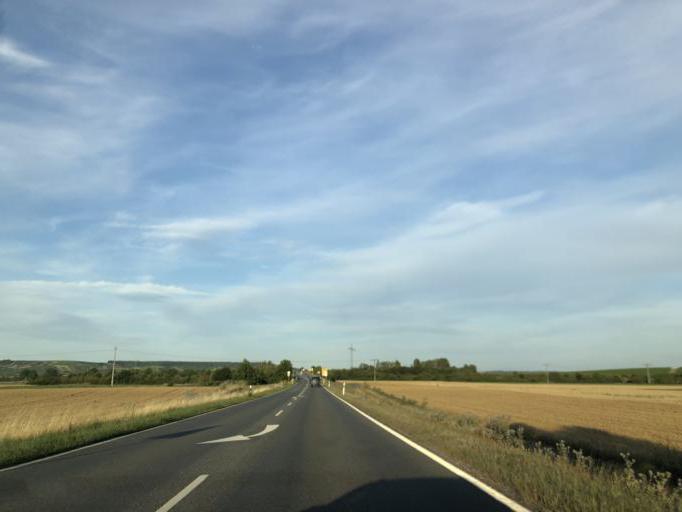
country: DE
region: Rheinland-Pfalz
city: Gensingen
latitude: 49.8853
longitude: 7.9266
